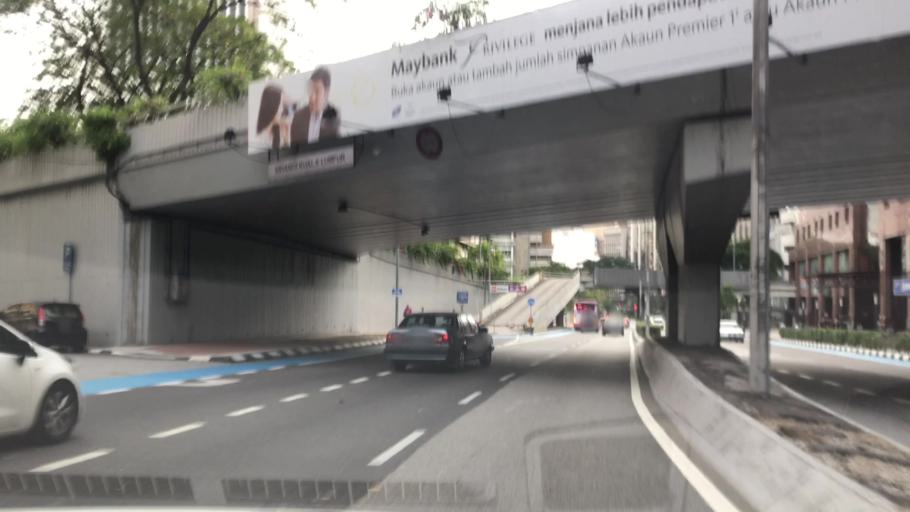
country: MY
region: Kuala Lumpur
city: Kuala Lumpur
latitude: 3.1490
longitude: 101.7015
